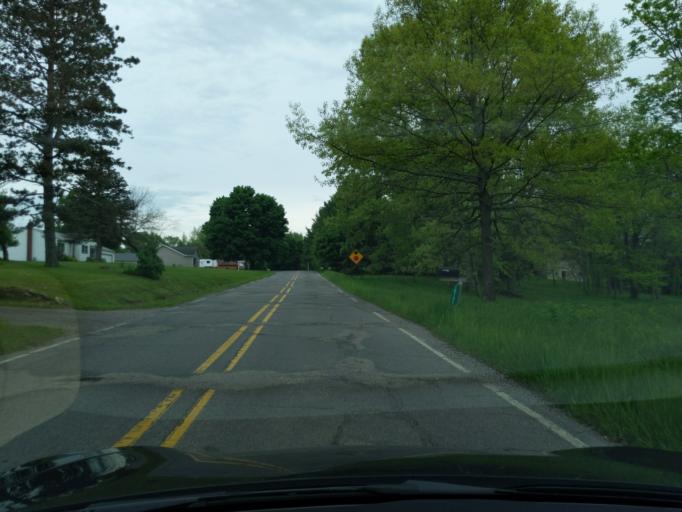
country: US
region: Michigan
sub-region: Ingham County
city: Leslie
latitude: 42.3822
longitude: -84.3295
